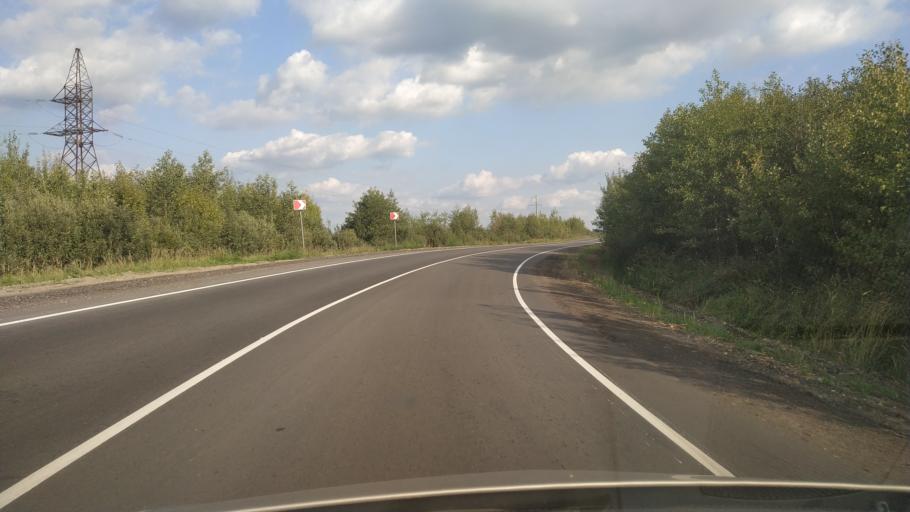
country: RU
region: Moskovskaya
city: Vereya
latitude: 55.7253
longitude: 39.0464
